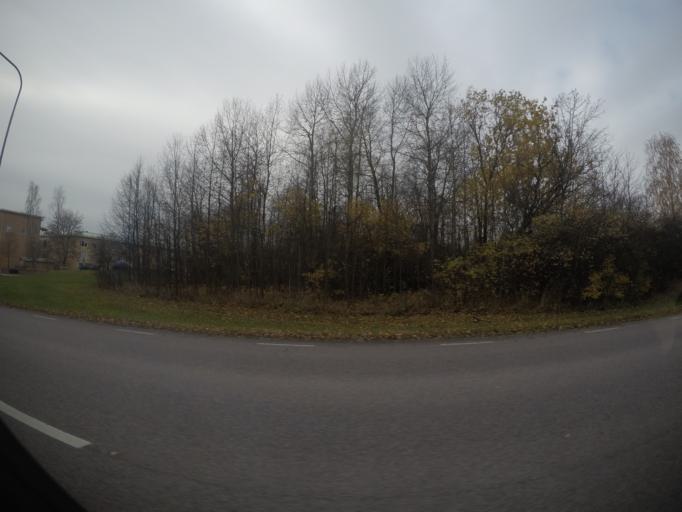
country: SE
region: Vaestmanland
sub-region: Vasteras
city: Vasteras
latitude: 59.6233
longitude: 16.5108
